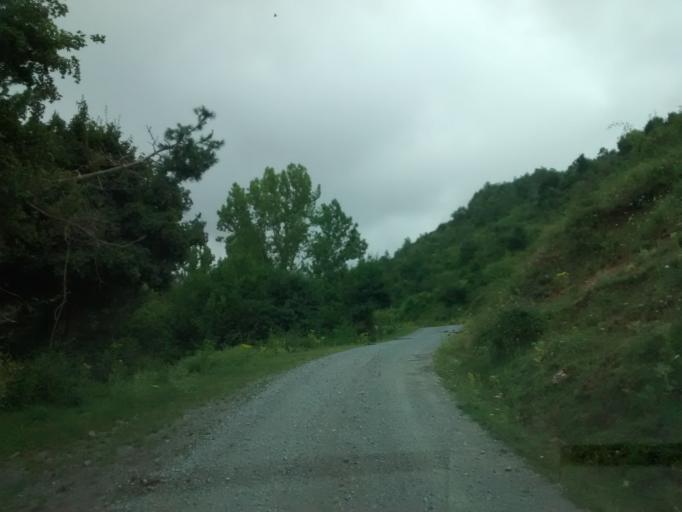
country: ES
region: La Rioja
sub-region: Provincia de La Rioja
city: Ajamil
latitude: 42.1619
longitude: -2.4855
